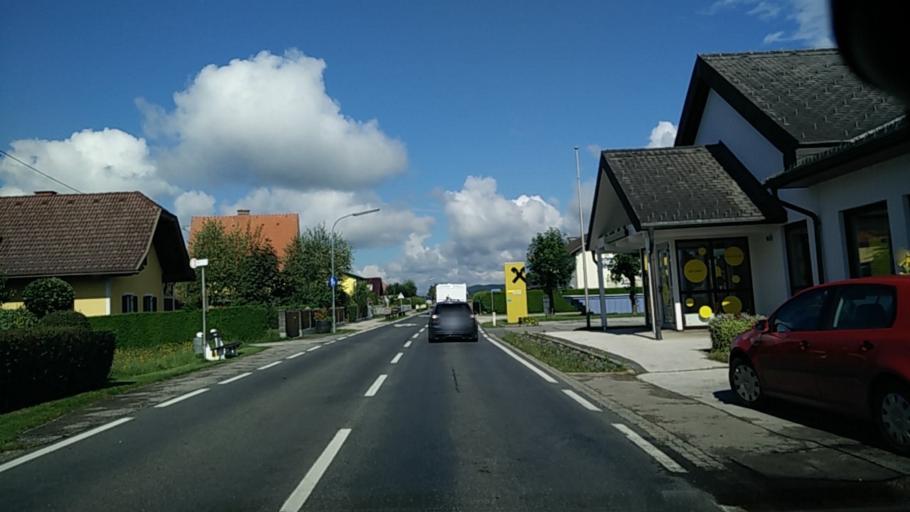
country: AT
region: Carinthia
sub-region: Politischer Bezirk Klagenfurt Land
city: Grafenstein
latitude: 46.6339
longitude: 14.5354
